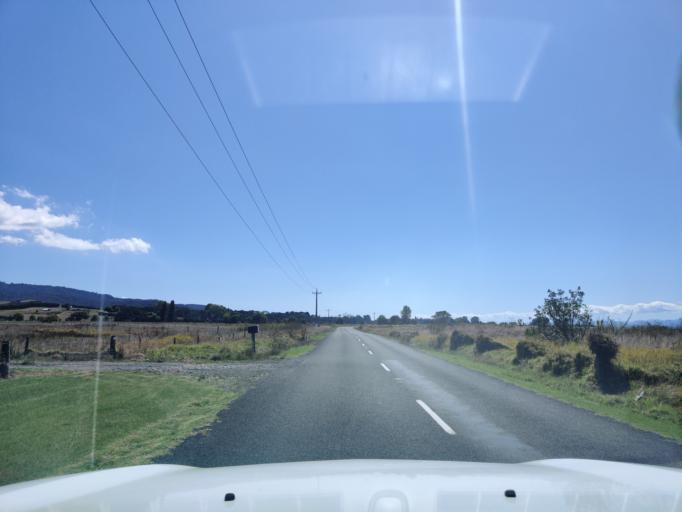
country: NZ
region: Waikato
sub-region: Thames-Coromandel District
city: Thames
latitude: -37.0715
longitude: 175.2958
